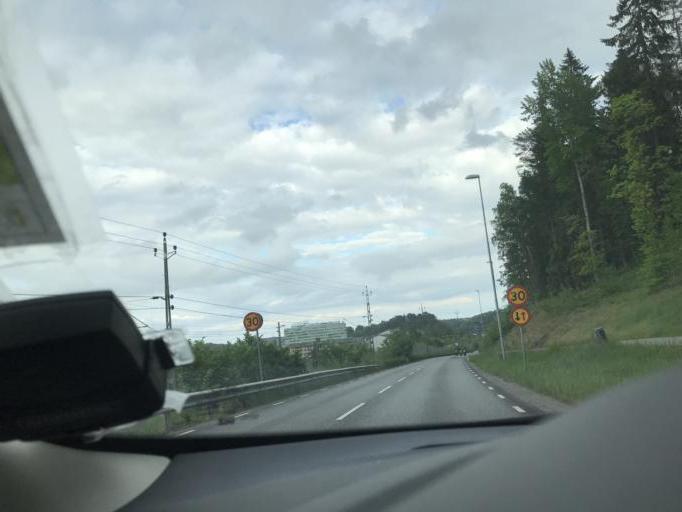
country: SE
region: Stockholm
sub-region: Botkyrka Kommun
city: Tumba
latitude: 59.2002
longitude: 17.8227
